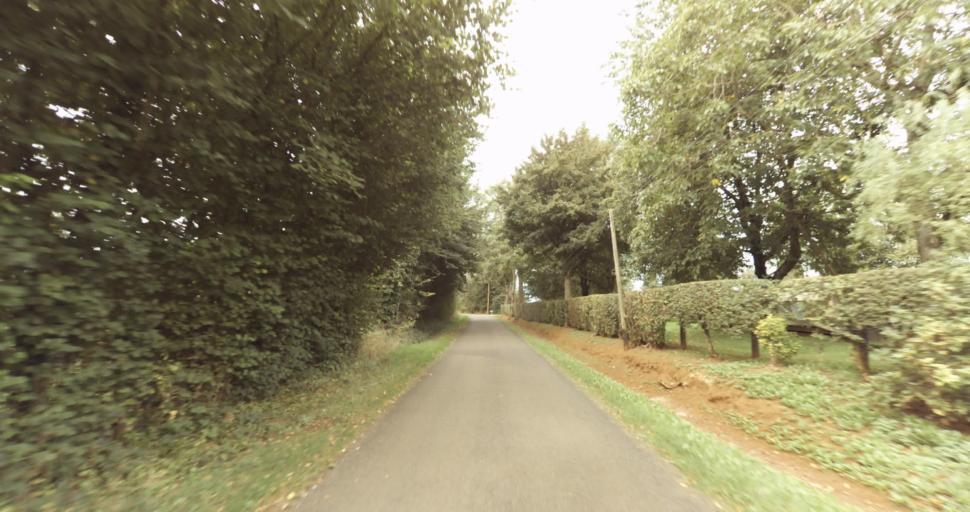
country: FR
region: Lower Normandy
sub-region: Departement de l'Orne
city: Gace
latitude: 48.7572
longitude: 0.3254
